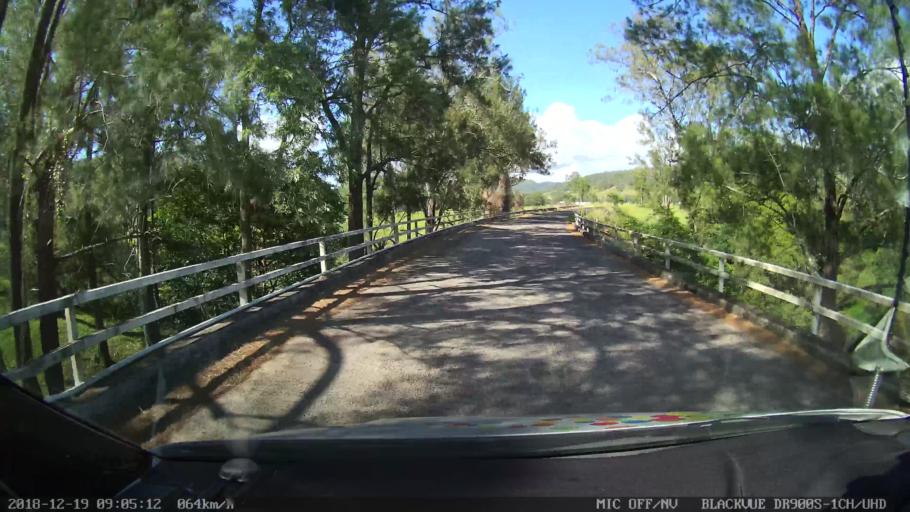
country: AU
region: New South Wales
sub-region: Kyogle
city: Kyogle
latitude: -28.4627
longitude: 152.9451
